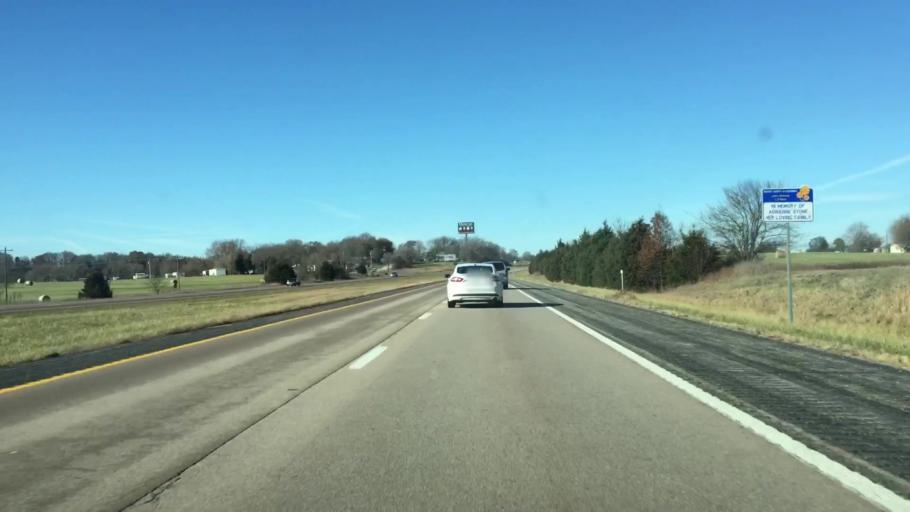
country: US
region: Missouri
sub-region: Miller County
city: Eldon
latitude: 38.3681
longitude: -92.5130
